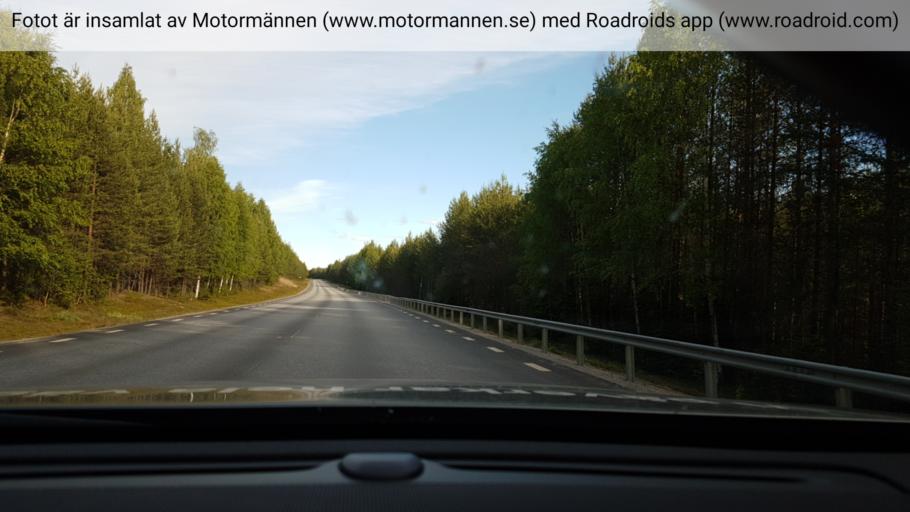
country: SE
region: Vaesterbotten
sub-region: Vindelns Kommun
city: Vindeln
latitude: 64.1501
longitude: 19.8604
